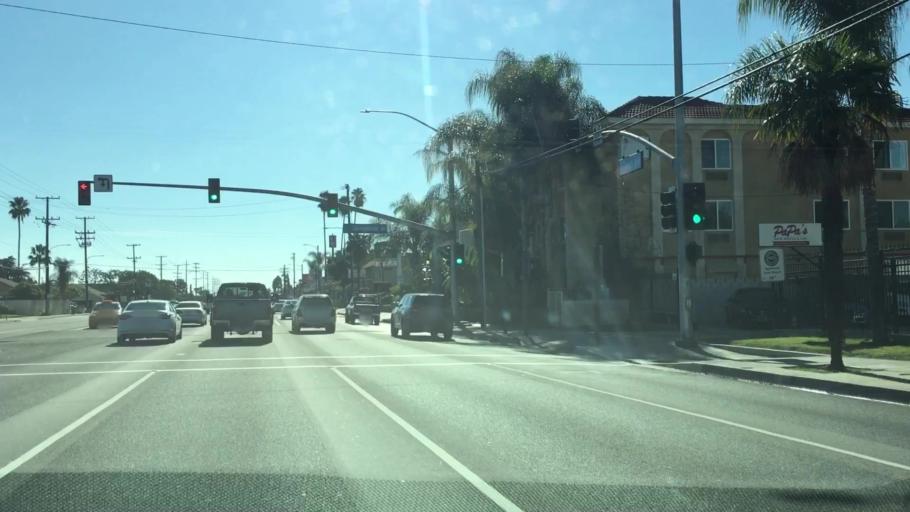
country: US
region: California
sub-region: Orange County
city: Stanton
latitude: 33.8217
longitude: -117.9934
